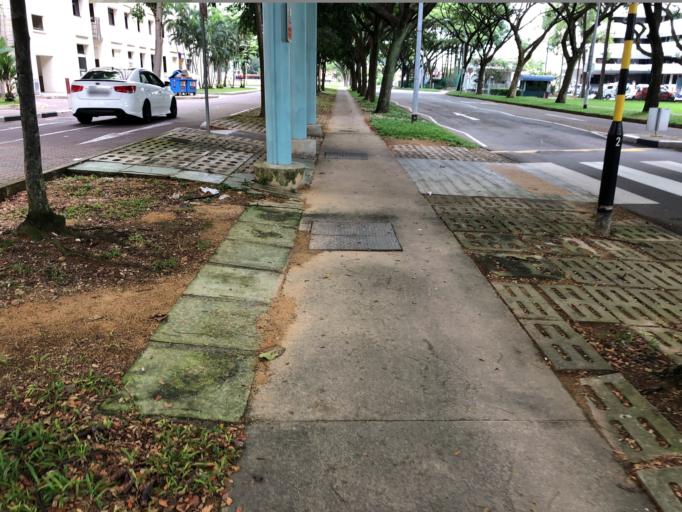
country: SG
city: Singapore
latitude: 1.3285
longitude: 103.8598
